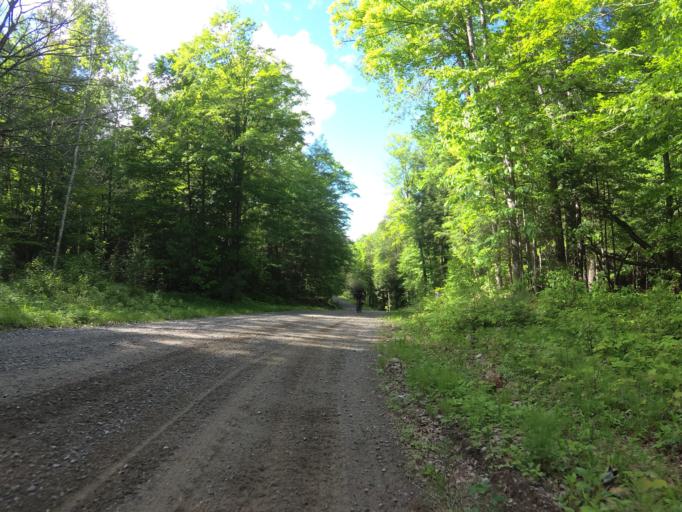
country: CA
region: Ontario
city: Renfrew
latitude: 45.1749
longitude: -76.8856
